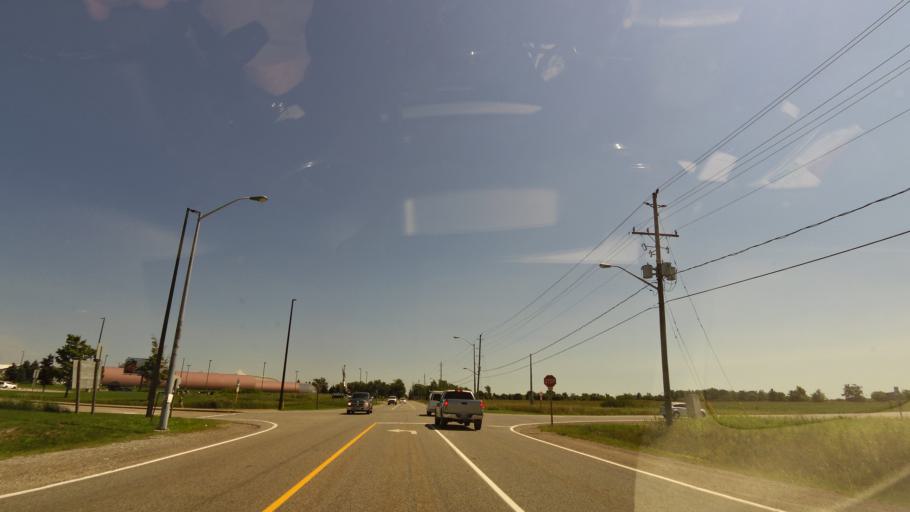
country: CA
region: Ontario
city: Ancaster
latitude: 43.1597
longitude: -79.9289
